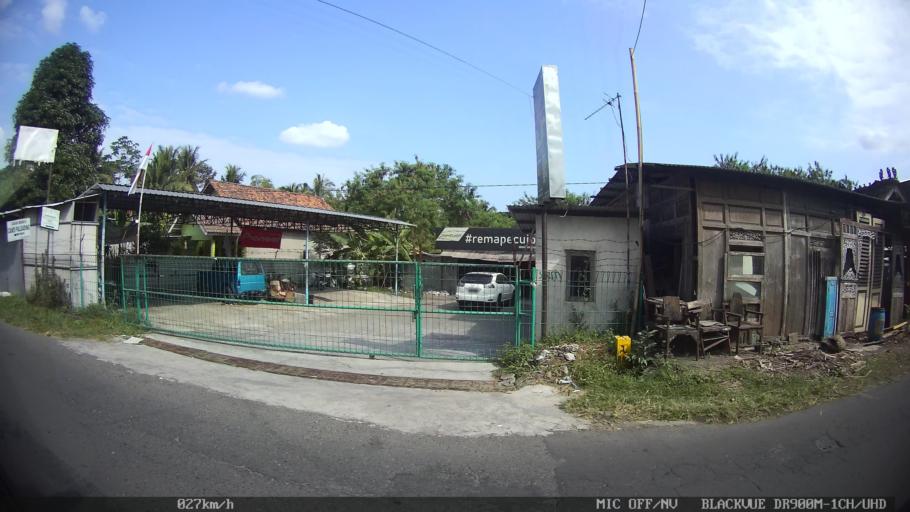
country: ID
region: Daerah Istimewa Yogyakarta
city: Depok
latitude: -7.7286
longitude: 110.4105
